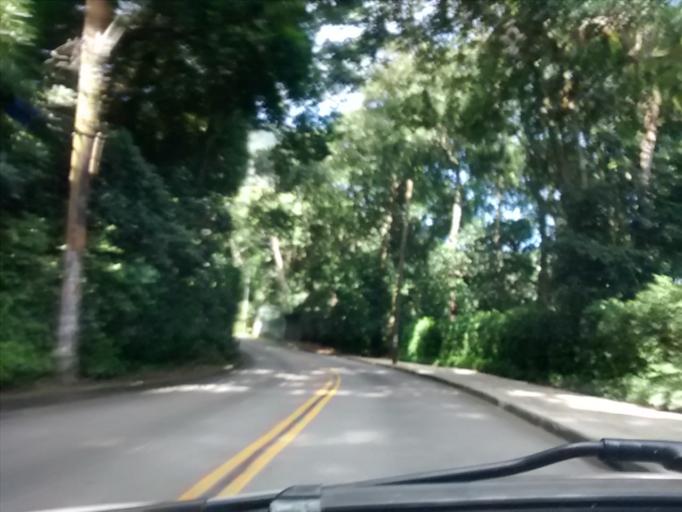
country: BR
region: Rio de Janeiro
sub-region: Rio De Janeiro
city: Rio de Janeiro
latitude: -22.9928
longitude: -43.2747
